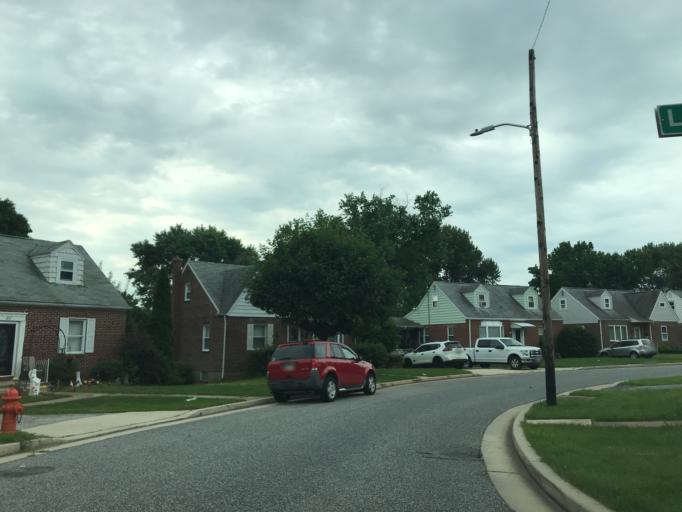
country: US
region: Maryland
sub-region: Baltimore County
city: Overlea
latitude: 39.3633
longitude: -76.5158
